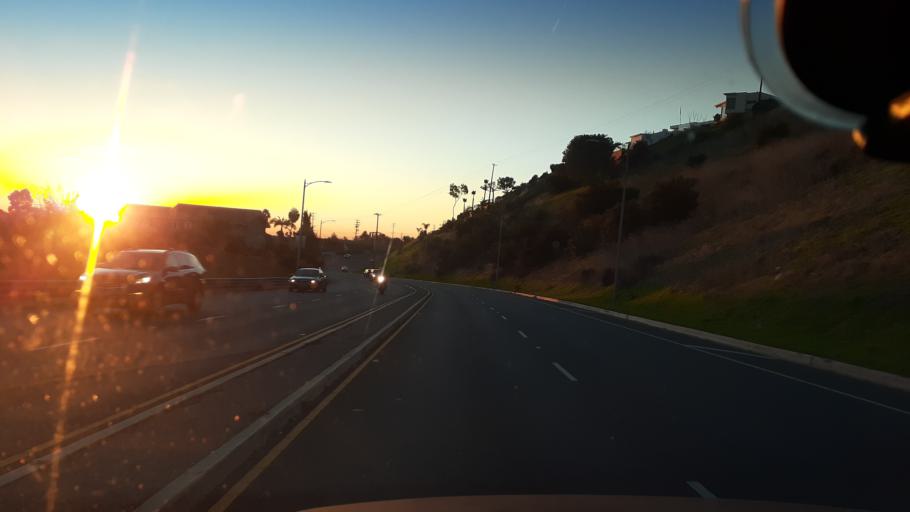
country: US
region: California
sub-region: Los Angeles County
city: San Pedro
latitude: 33.7308
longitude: -118.3143
